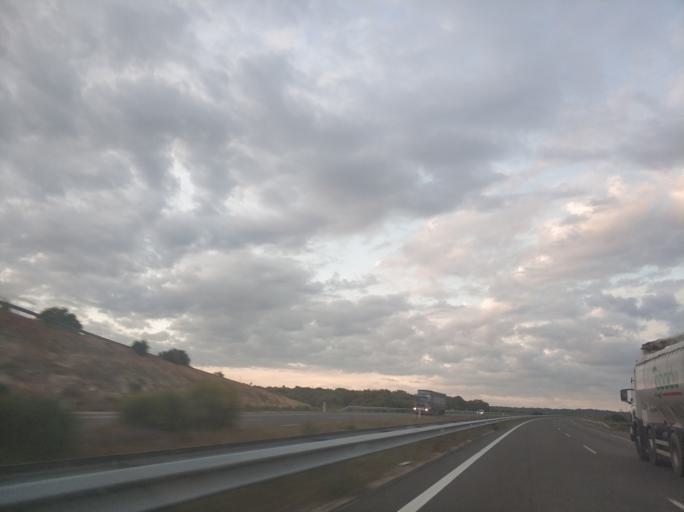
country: ES
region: Castille and Leon
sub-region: Provincia de Salamanca
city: Mozarbez
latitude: 40.8420
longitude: -5.6389
